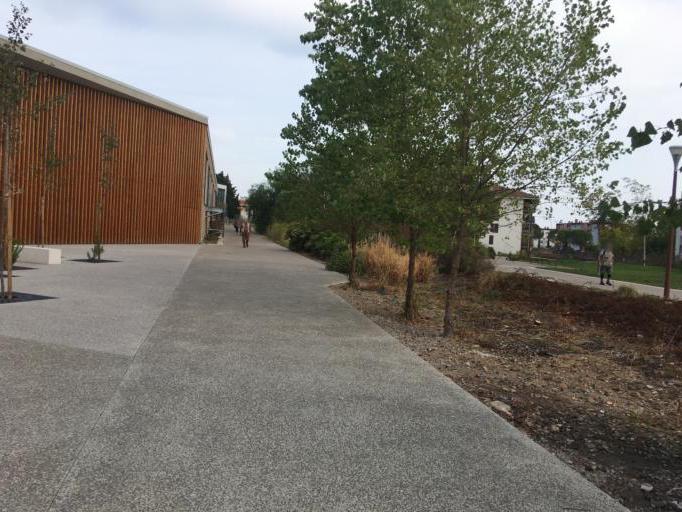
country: FR
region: Provence-Alpes-Cote d'Azur
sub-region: Departement du Var
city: Draguignan
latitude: 43.5348
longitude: 6.4743
